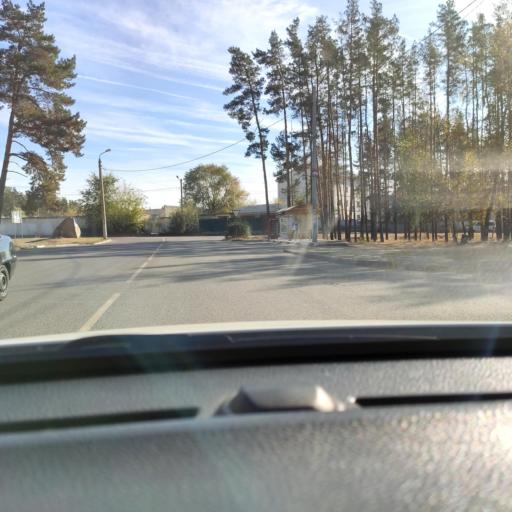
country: RU
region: Voronezj
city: Pridonskoy
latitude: 51.6807
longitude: 39.0937
